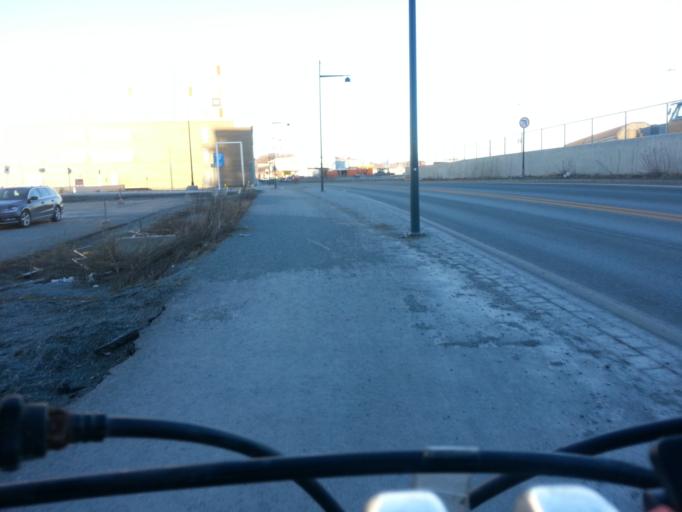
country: NO
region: Sor-Trondelag
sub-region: Trondheim
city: Trondheim
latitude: 63.4375
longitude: 10.3995
